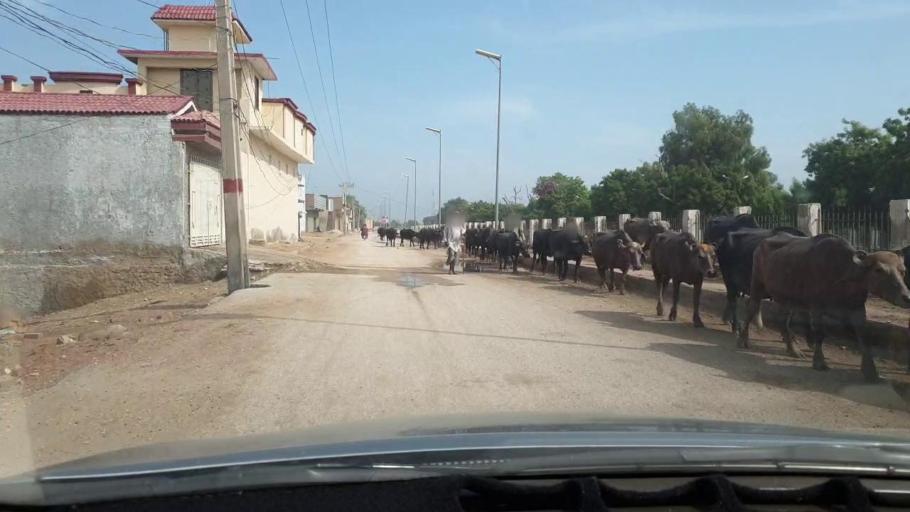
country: PK
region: Sindh
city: Khairpur
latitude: 27.5164
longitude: 68.7586
